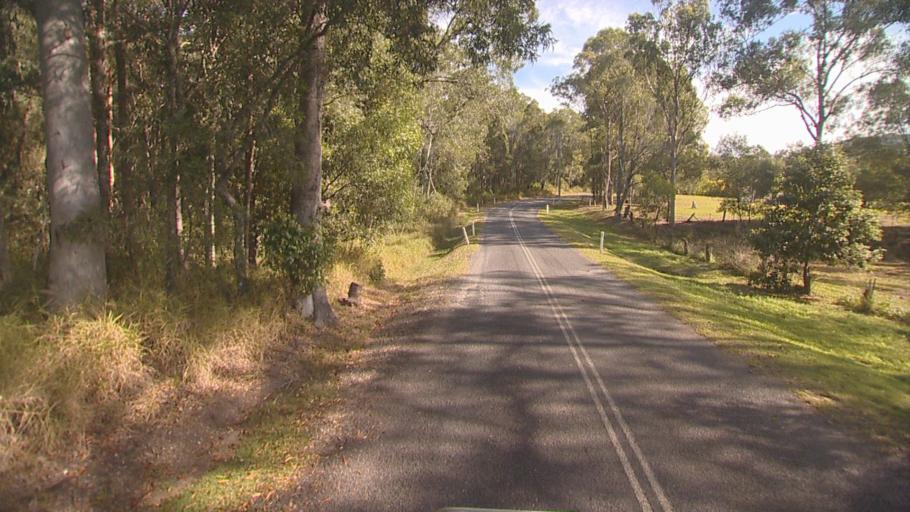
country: AU
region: Queensland
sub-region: Logan
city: Windaroo
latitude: -27.7777
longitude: 153.1829
